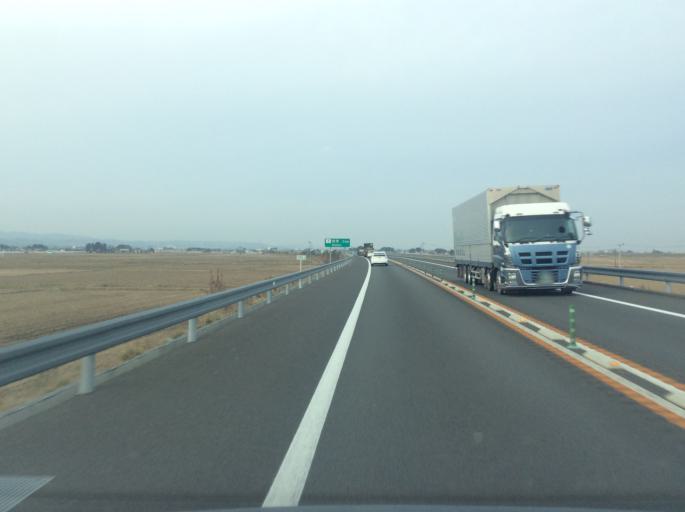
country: JP
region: Miyagi
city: Iwanuma
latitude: 38.0668
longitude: 140.8930
